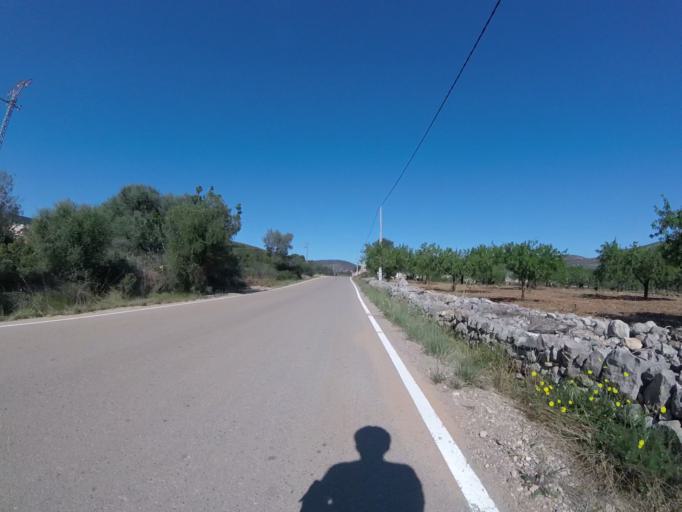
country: ES
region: Valencia
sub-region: Provincia de Castello
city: Santa Magdalena de Pulpis
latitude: 40.3635
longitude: 0.2801
